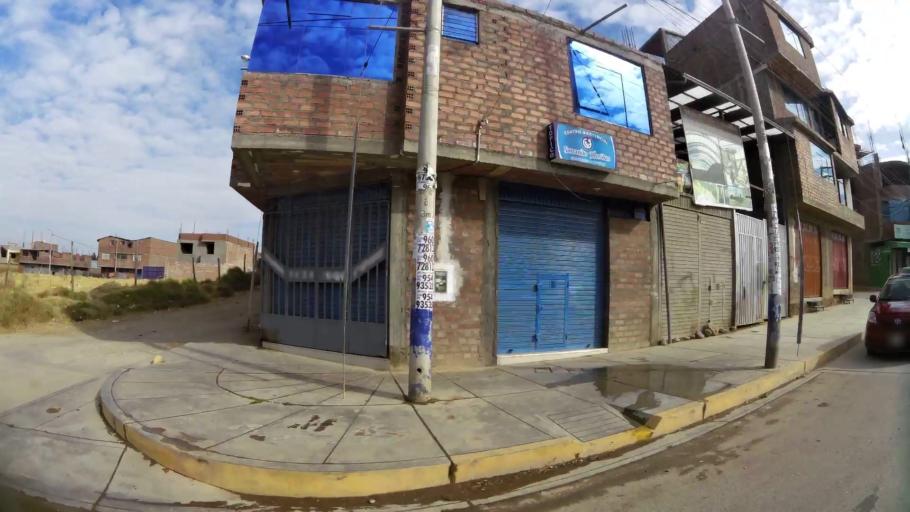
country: PE
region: Junin
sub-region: Provincia de Huancayo
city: Huancayo
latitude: -12.0526
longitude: -75.1953
